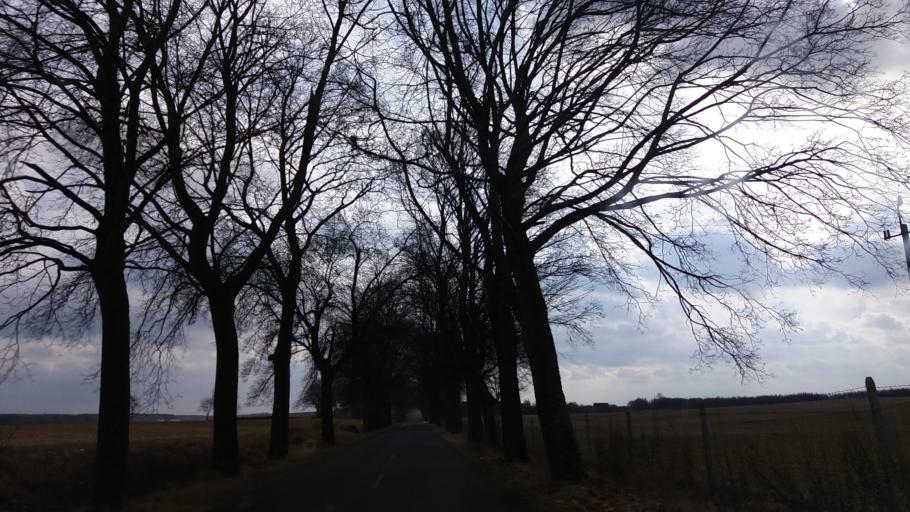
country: PL
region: West Pomeranian Voivodeship
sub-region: Powiat choszczenski
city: Drawno
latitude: 53.2454
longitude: 15.7283
